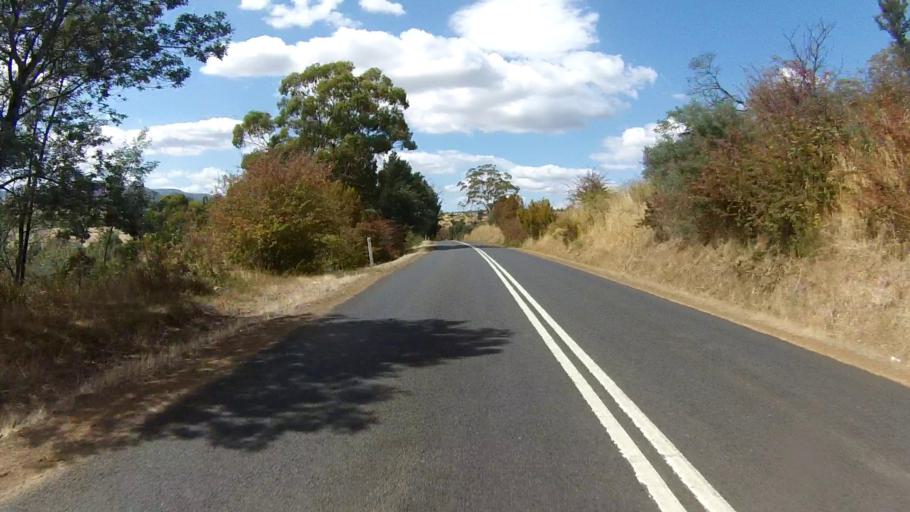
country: AU
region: Tasmania
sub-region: Derwent Valley
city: New Norfolk
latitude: -42.7329
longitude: 146.9080
